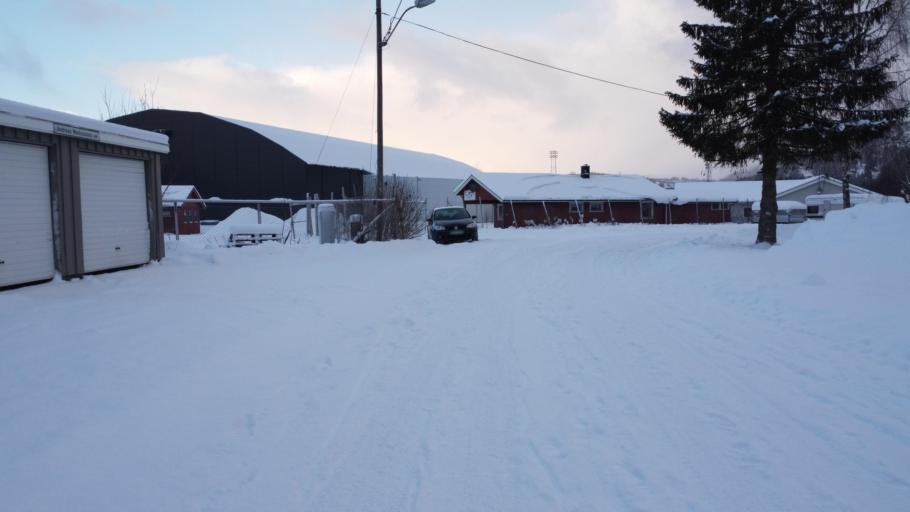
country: NO
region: Nordland
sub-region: Rana
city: Mo i Rana
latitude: 66.3206
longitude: 14.1623
